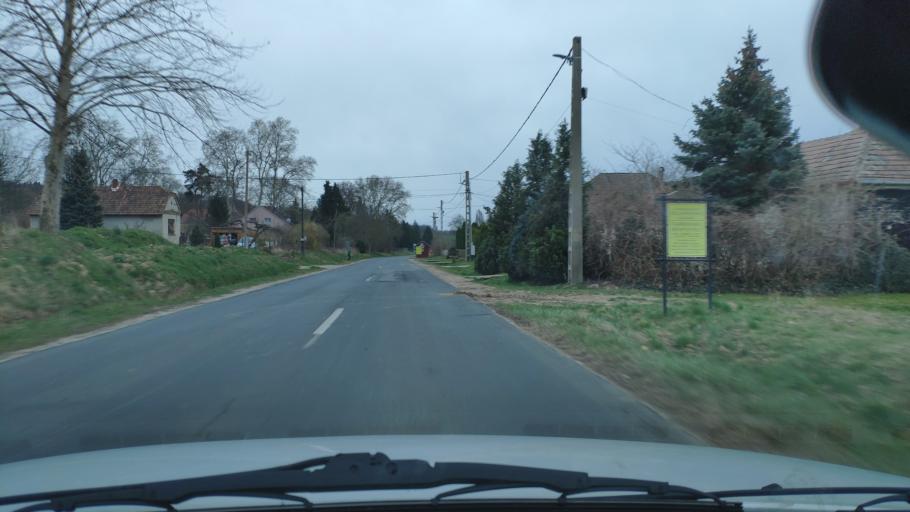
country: HU
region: Zala
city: Nagykanizsa
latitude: 46.5557
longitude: 16.9896
